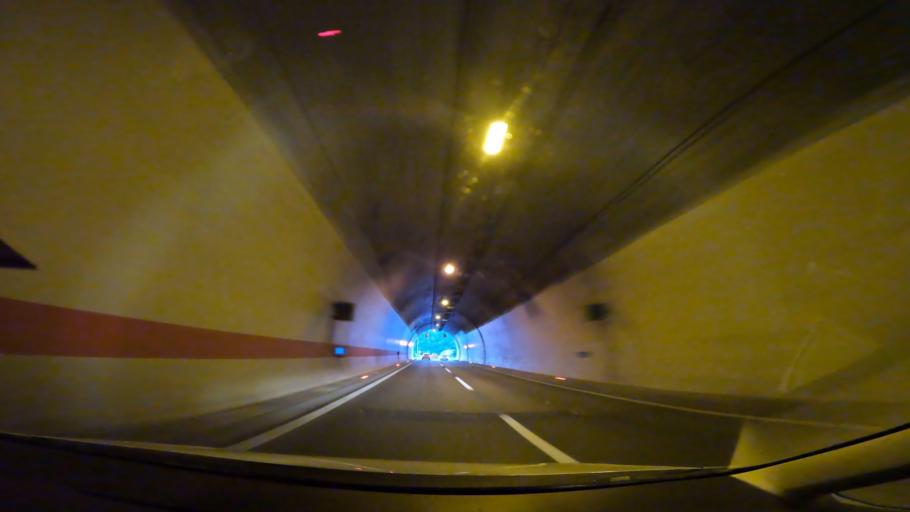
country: HR
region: Primorsko-Goranska
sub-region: Grad Delnice
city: Delnice
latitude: 45.3438
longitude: 14.7476
